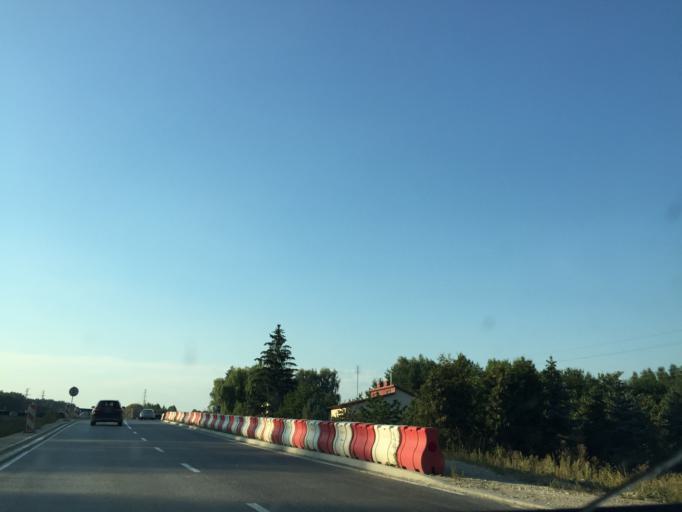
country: PL
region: Masovian Voivodeship
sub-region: Powiat grojecki
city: Grojec
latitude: 51.9121
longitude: 20.8560
